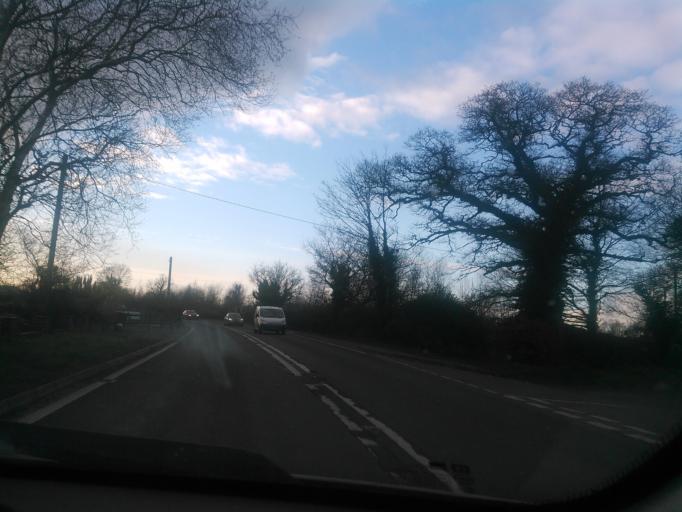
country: GB
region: England
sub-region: Shropshire
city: Stoke upon Tern
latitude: 52.8666
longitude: -2.5011
